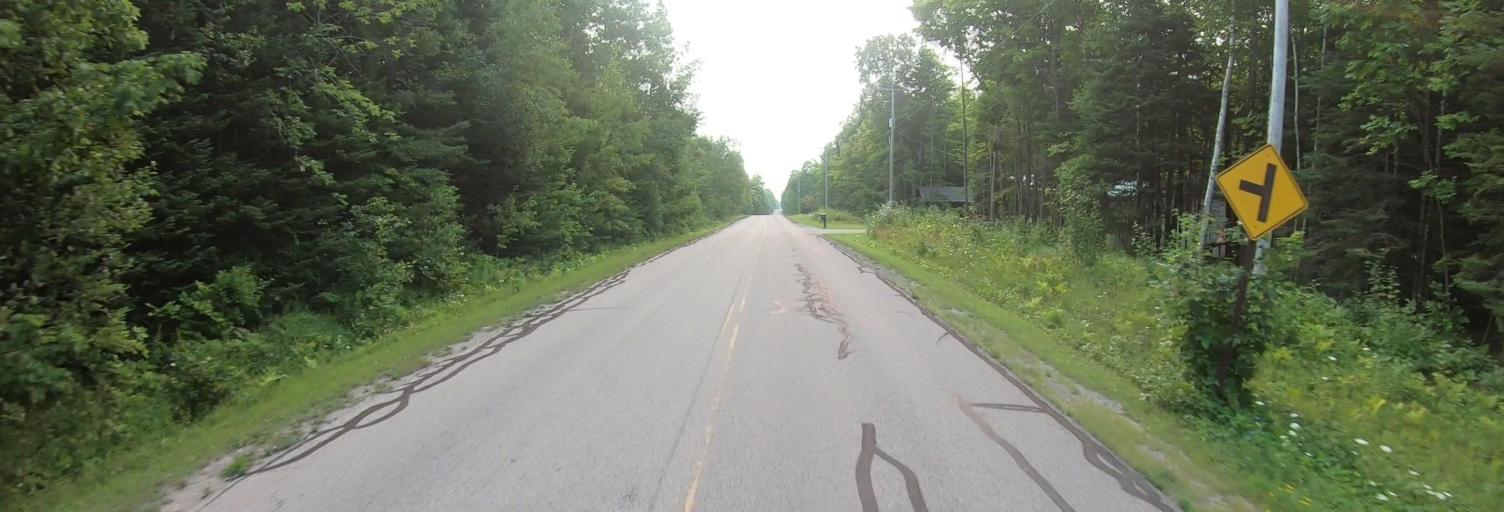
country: US
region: Michigan
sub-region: Mackinac County
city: Saint Ignace
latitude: 45.7649
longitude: -84.7557
